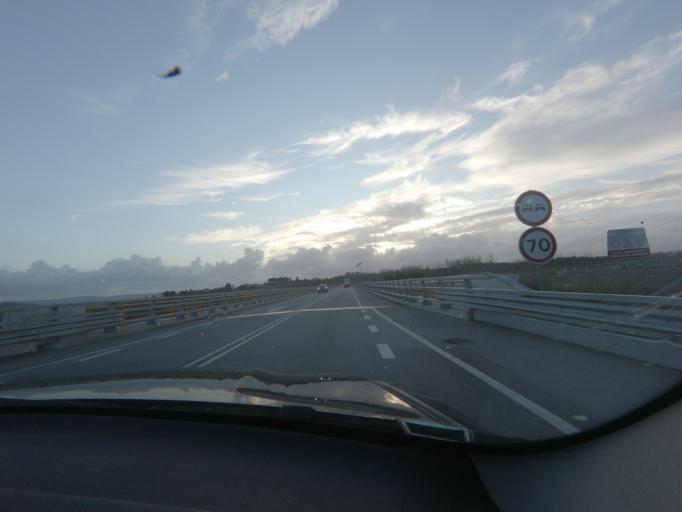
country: PT
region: Viseu
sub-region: Santa Comba Dao
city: Santa Comba Dao
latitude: 40.3474
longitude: -8.1791
